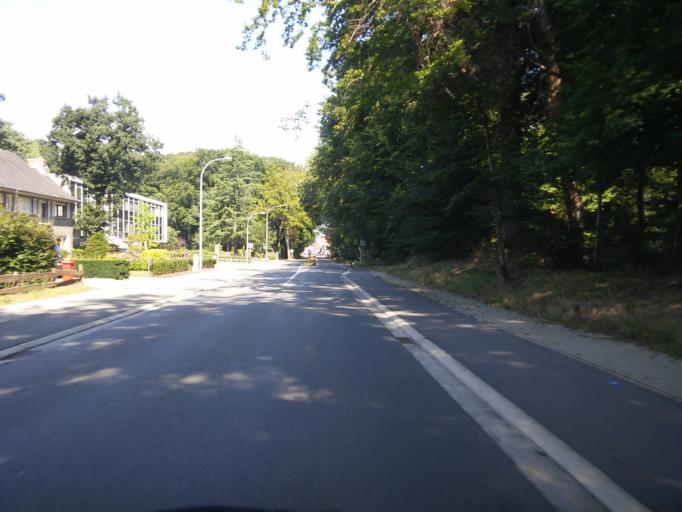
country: BE
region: Flanders
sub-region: Provincie Oost-Vlaanderen
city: Buggenhout
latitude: 51.0035
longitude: 4.2084
